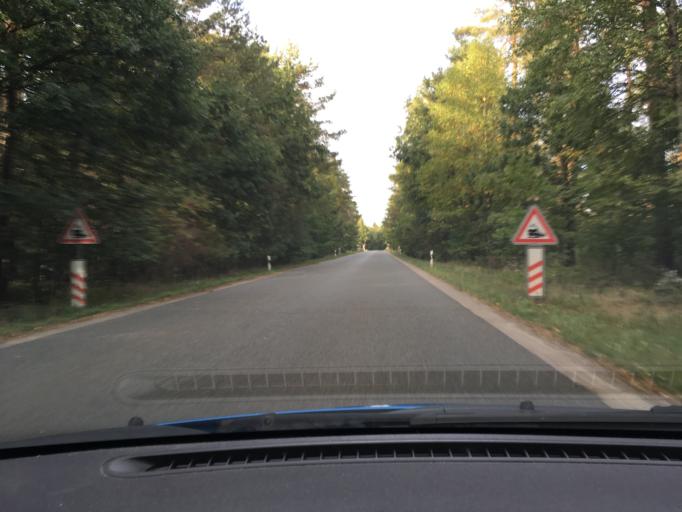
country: DE
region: Lower Saxony
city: Wietzendorf
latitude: 52.9384
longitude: 9.9080
